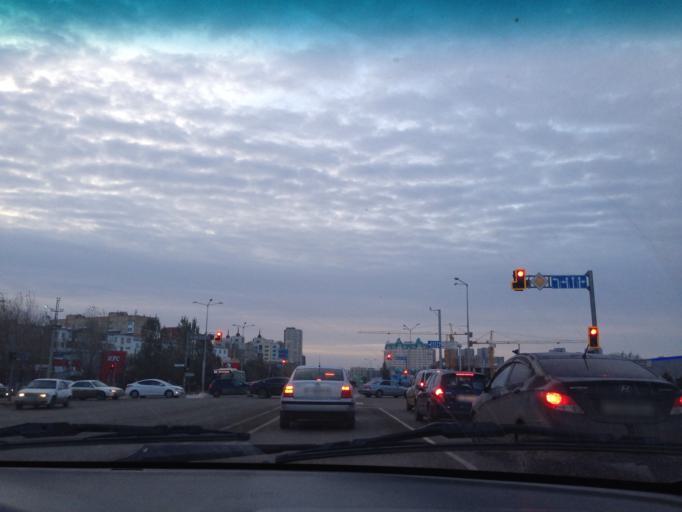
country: KZ
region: Astana Qalasy
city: Astana
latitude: 51.1465
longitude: 71.4596
